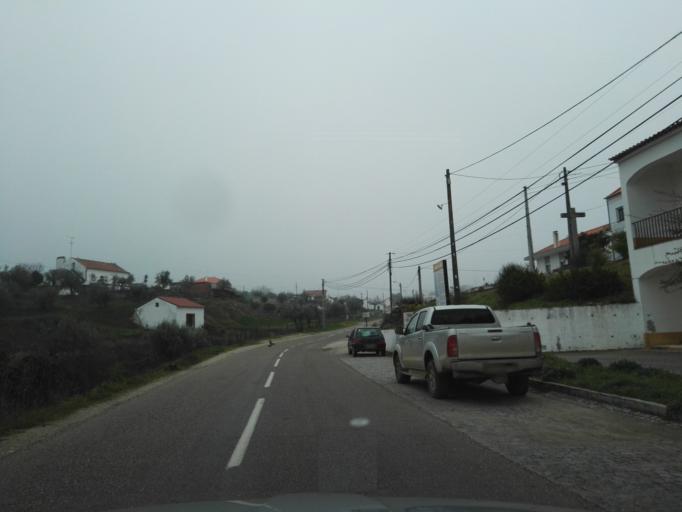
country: PT
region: Evora
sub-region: Montemor-O-Novo
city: Montemor-o-Novo
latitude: 38.8001
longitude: -8.2282
